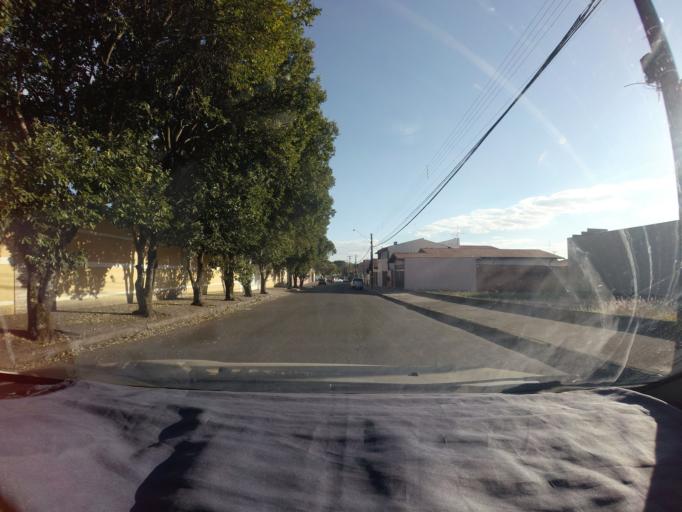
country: BR
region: Sao Paulo
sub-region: Piracicaba
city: Piracicaba
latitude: -22.7383
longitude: -47.5970
